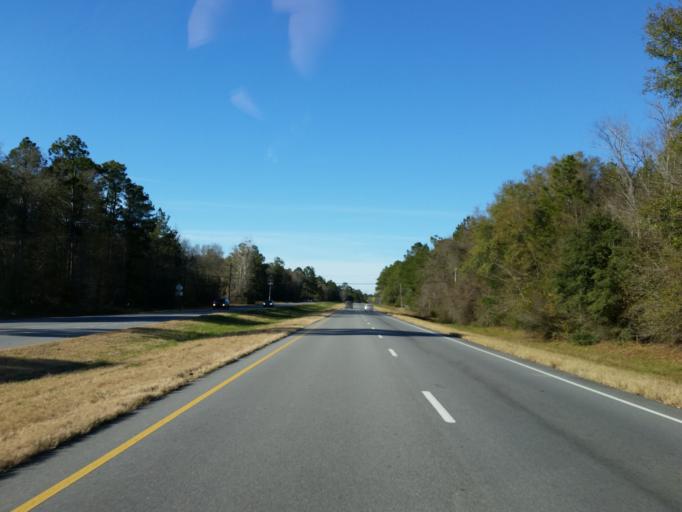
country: US
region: Georgia
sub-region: Lowndes County
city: Valdosta
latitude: 30.7108
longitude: -83.2135
